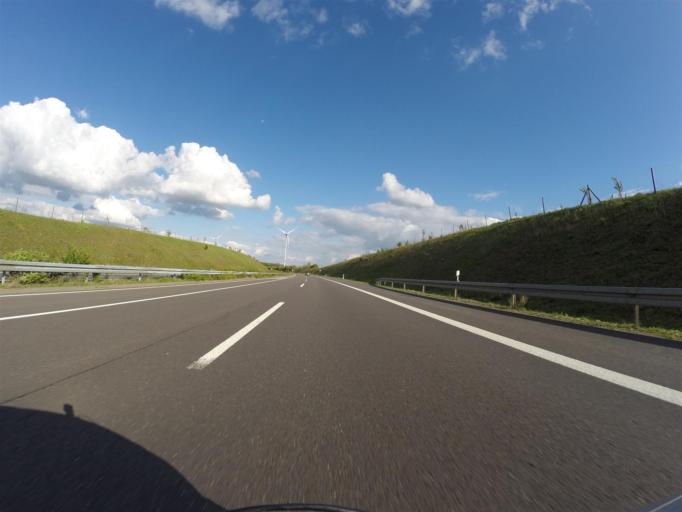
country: DE
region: Saarland
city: Perl
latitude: 49.4701
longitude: 6.4398
